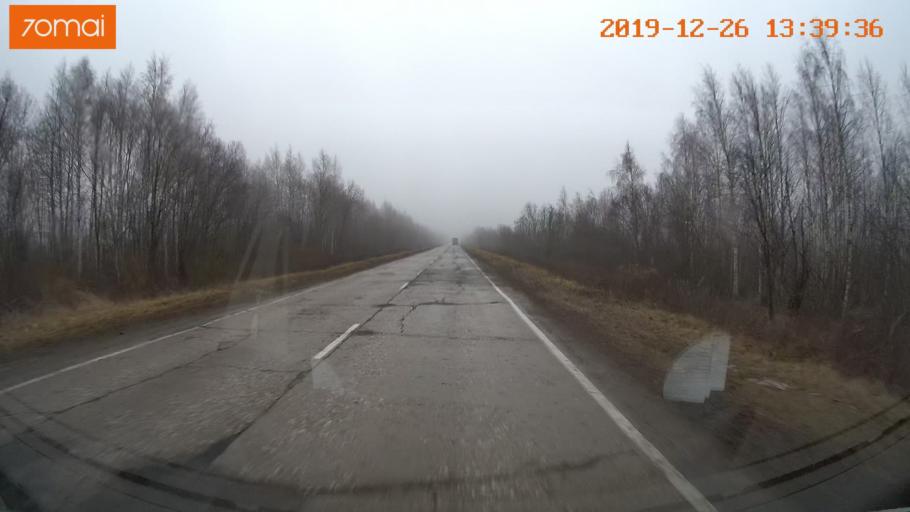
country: RU
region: Vologda
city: Sheksna
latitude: 58.7504
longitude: 38.4145
